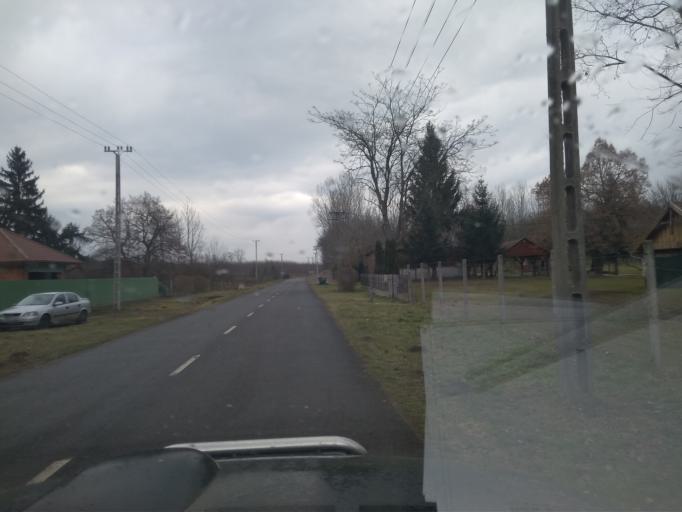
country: HU
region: Szabolcs-Szatmar-Bereg
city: Nyirpazony
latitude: 48.0288
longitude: 21.7800
